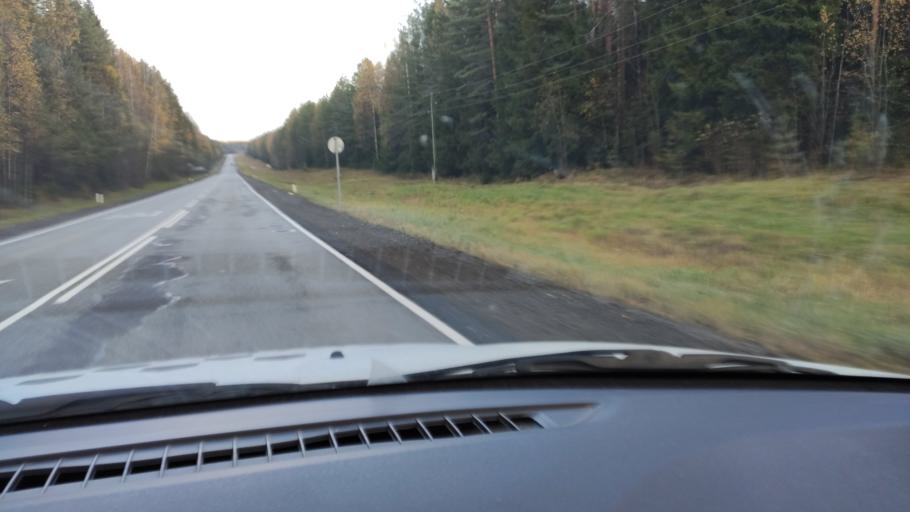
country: RU
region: Kirov
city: Belaya Kholunitsa
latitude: 58.9050
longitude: 50.9605
